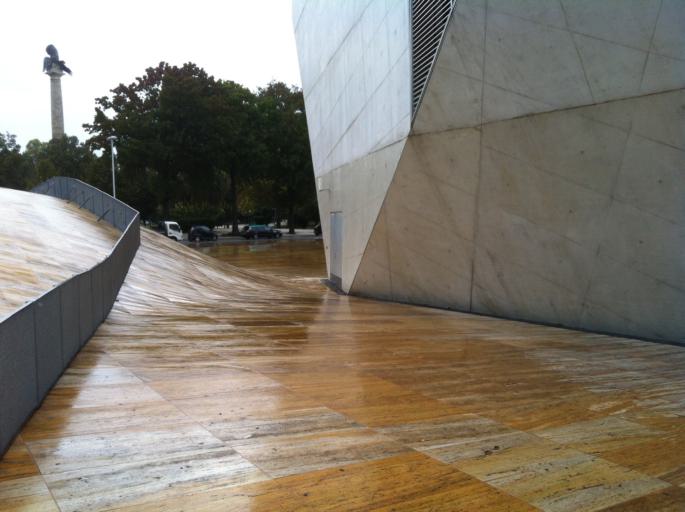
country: PT
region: Porto
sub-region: Porto
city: Porto
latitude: 41.1591
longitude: -8.6304
